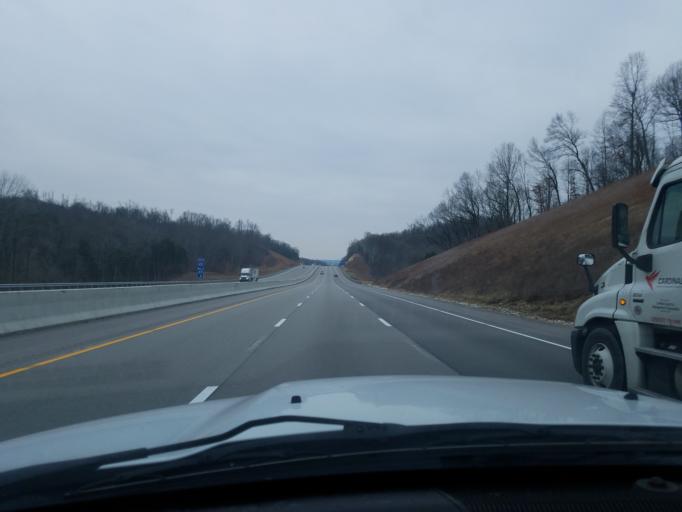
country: US
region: Kentucky
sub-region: Hart County
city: Munfordville
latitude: 37.3129
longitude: -85.9045
